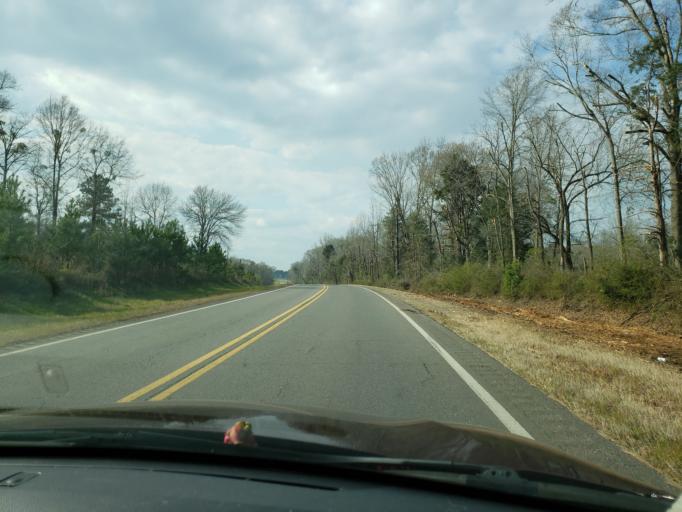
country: US
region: Alabama
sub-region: Hale County
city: Greensboro
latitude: 32.7080
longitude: -87.6085
